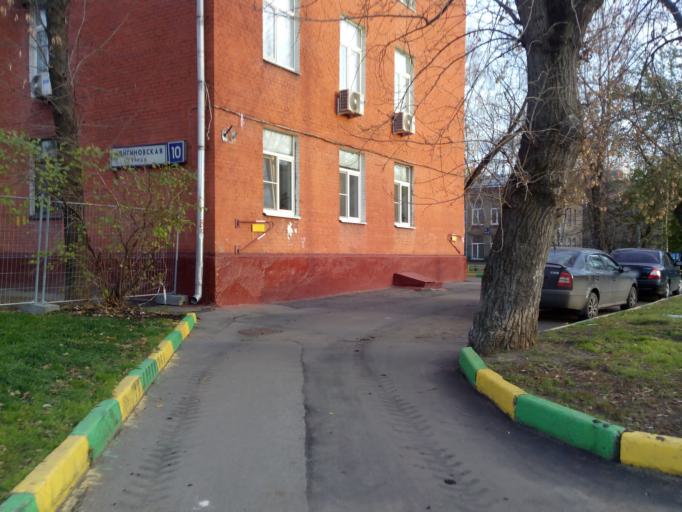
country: RU
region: Moscow
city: Lefortovo
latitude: 55.7687
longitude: 37.7118
